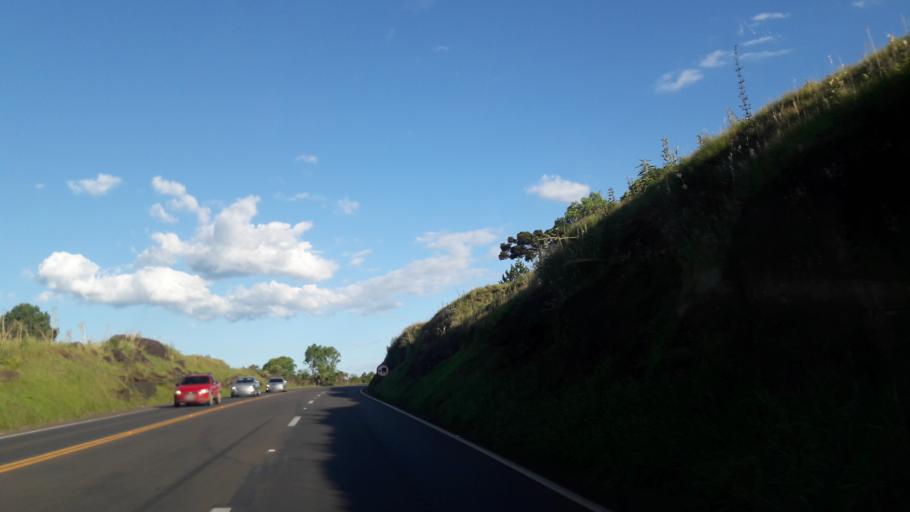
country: BR
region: Parana
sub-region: Guarapuava
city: Guarapuava
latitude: -25.3593
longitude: -51.3549
